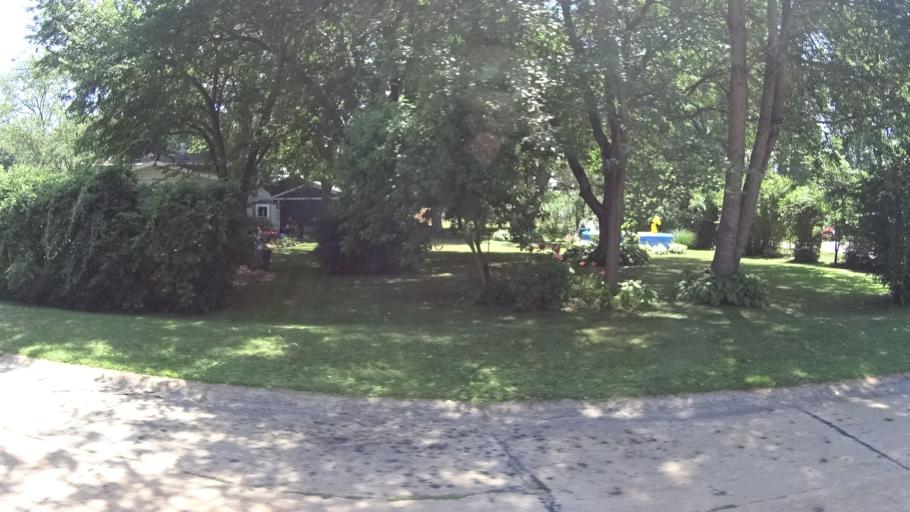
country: US
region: Ohio
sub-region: Erie County
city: Sandusky
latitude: 41.3892
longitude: -82.6708
